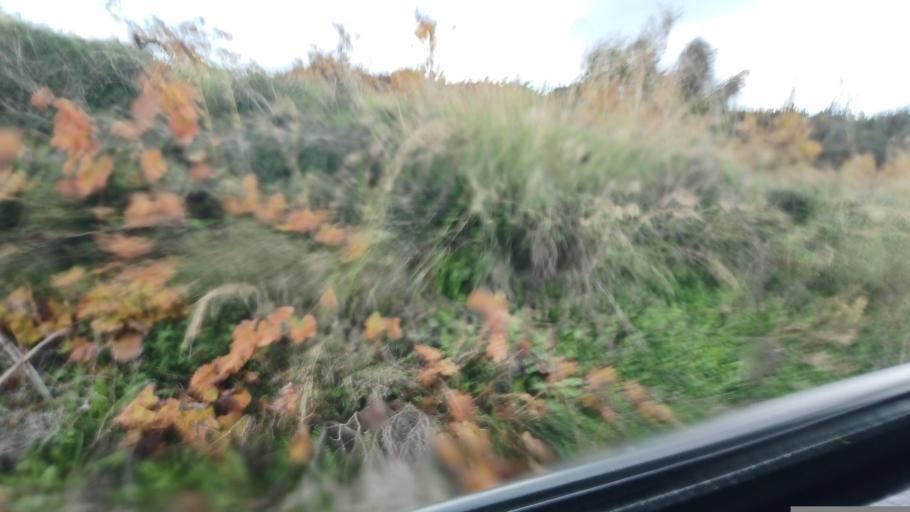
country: CY
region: Pafos
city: Mesogi
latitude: 34.8338
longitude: 32.5253
